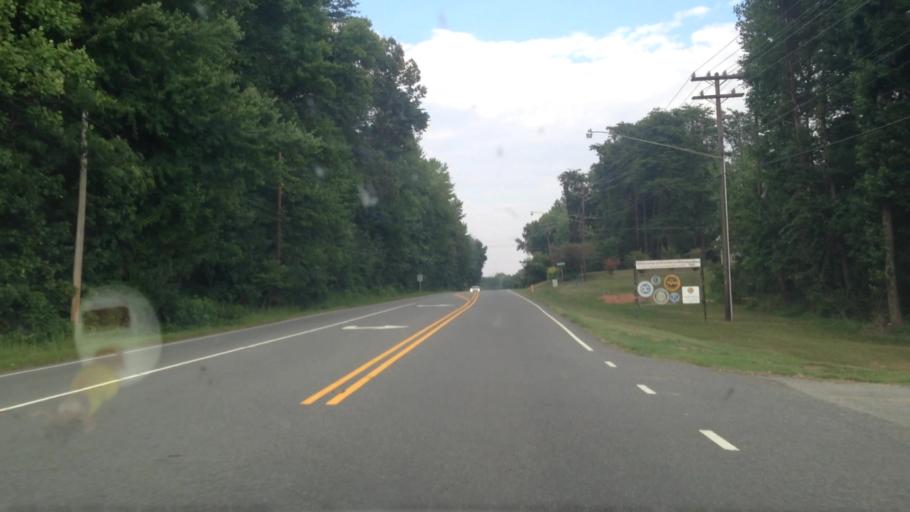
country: US
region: North Carolina
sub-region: Forsyth County
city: Kernersville
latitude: 36.1332
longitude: -80.0920
